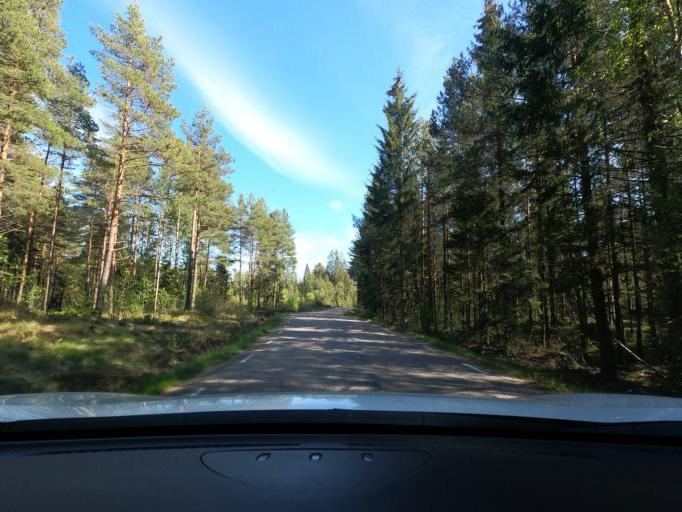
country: SE
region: Vaestra Goetaland
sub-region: Harryda Kommun
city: Hindas
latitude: 57.6635
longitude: 12.3522
